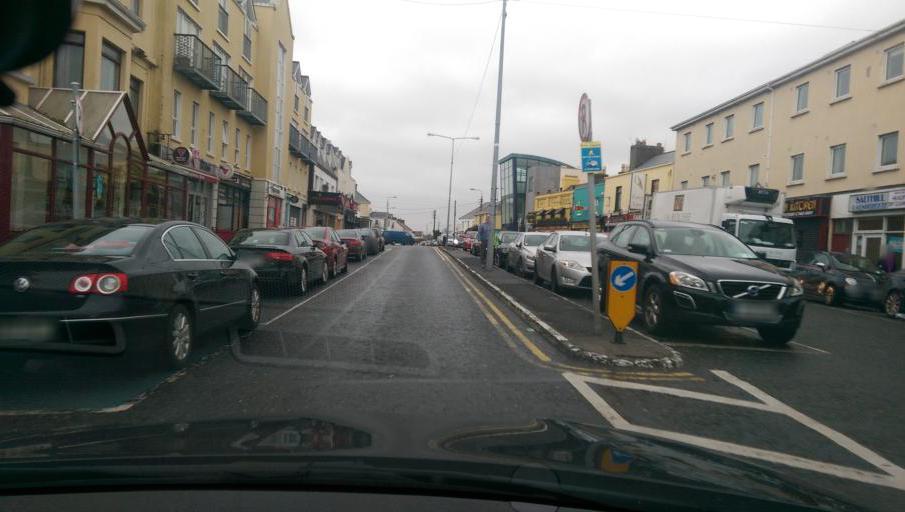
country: IE
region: Connaught
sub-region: County Galway
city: Gaillimh
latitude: 53.2607
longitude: -9.0752
